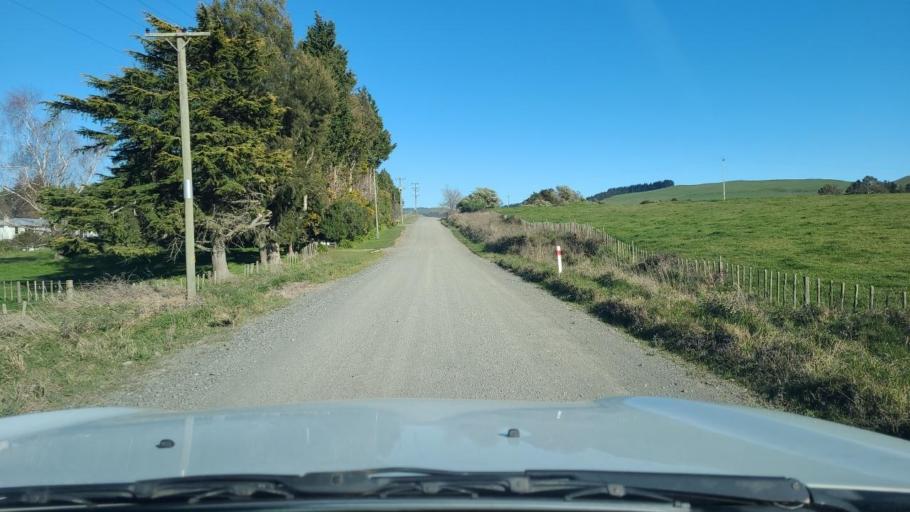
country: NZ
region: Hawke's Bay
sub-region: Napier City
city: Taradale
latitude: -39.3899
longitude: 176.5485
